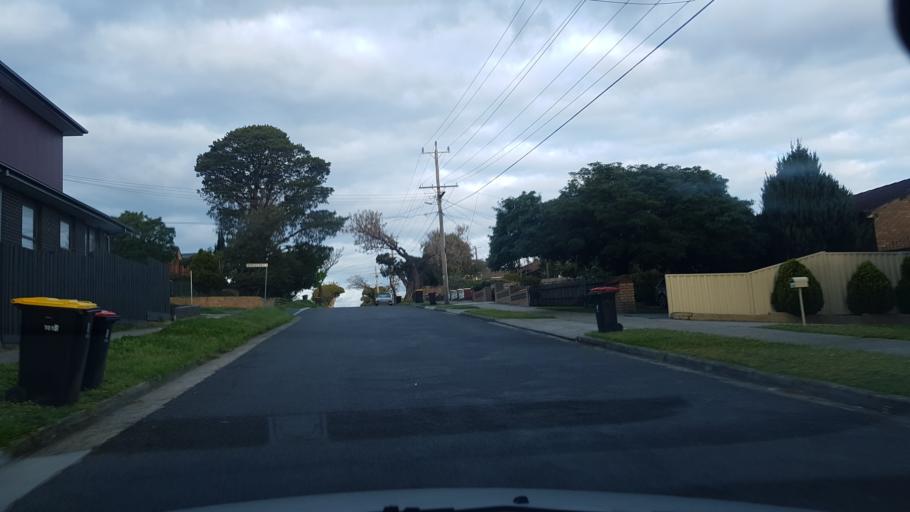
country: AU
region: Victoria
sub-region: Greater Dandenong
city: Springvale
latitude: -37.9454
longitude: 145.1360
